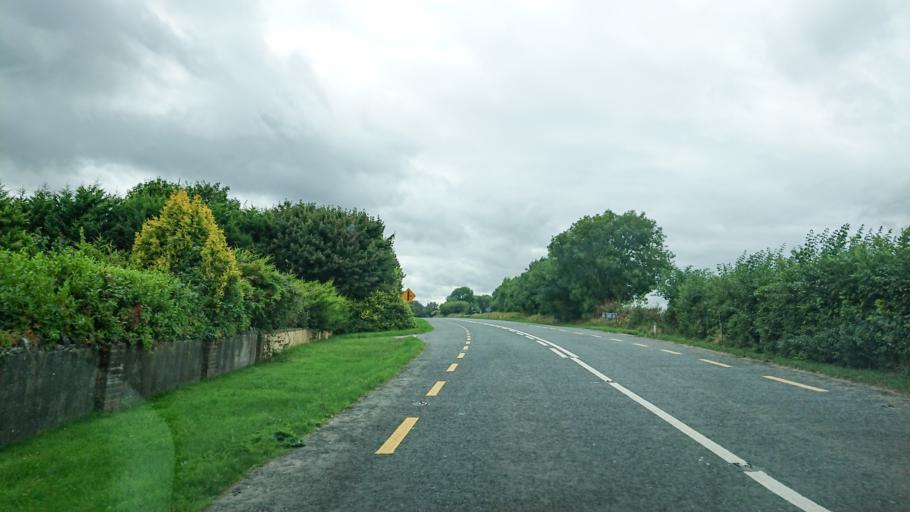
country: IE
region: Munster
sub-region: County Cork
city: Mallow
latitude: 52.1533
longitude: -8.5862
